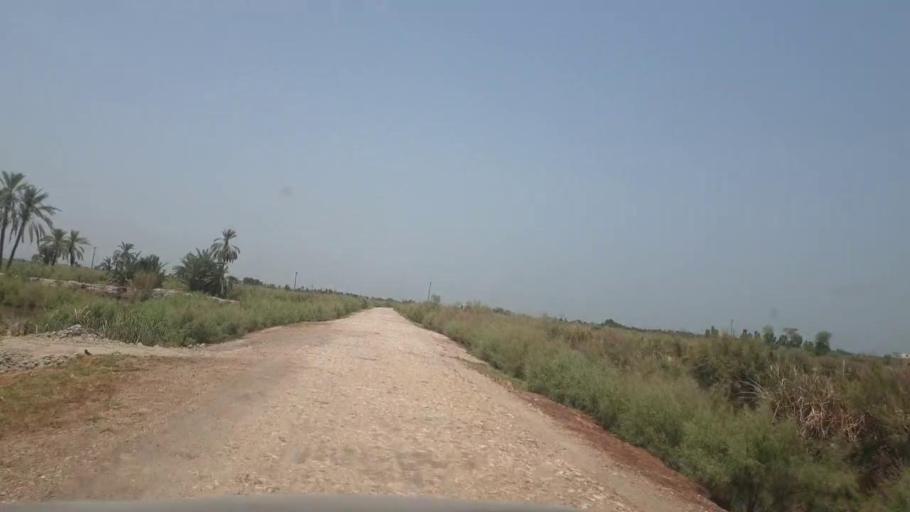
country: PK
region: Sindh
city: Lakhi
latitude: 27.8458
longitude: 68.6255
